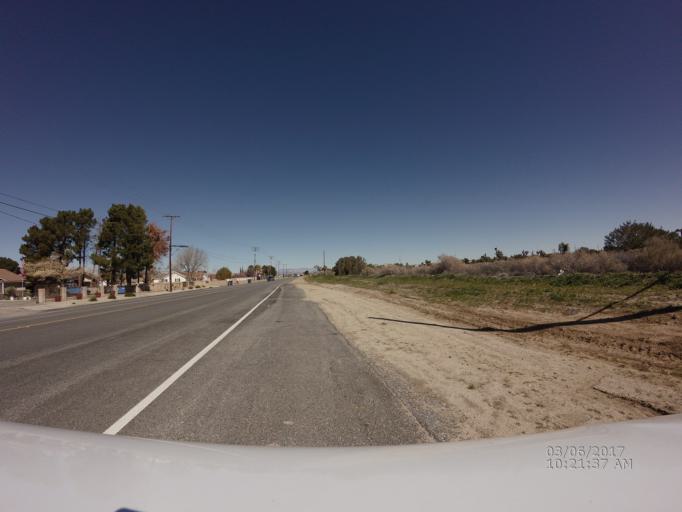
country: US
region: California
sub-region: Los Angeles County
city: Quartz Hill
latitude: 34.6721
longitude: -118.2188
